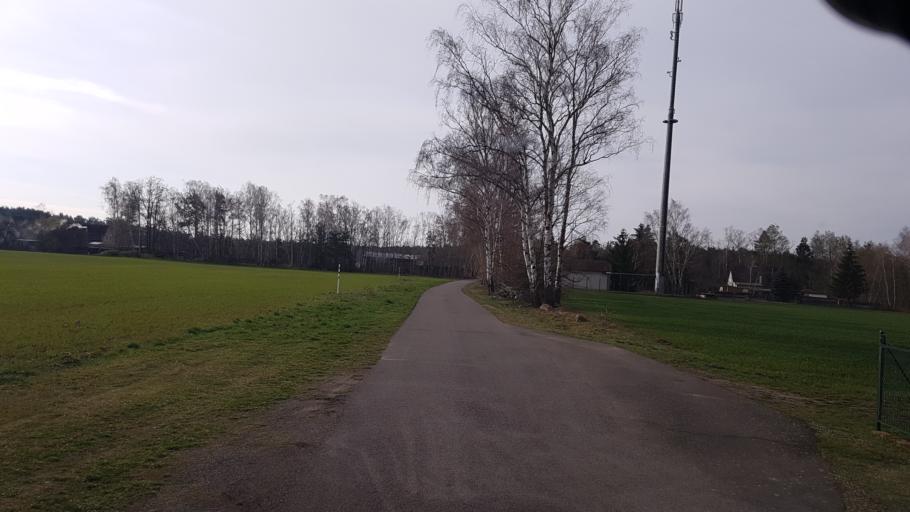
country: DE
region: Brandenburg
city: Bronkow
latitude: 51.7080
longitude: 13.8877
